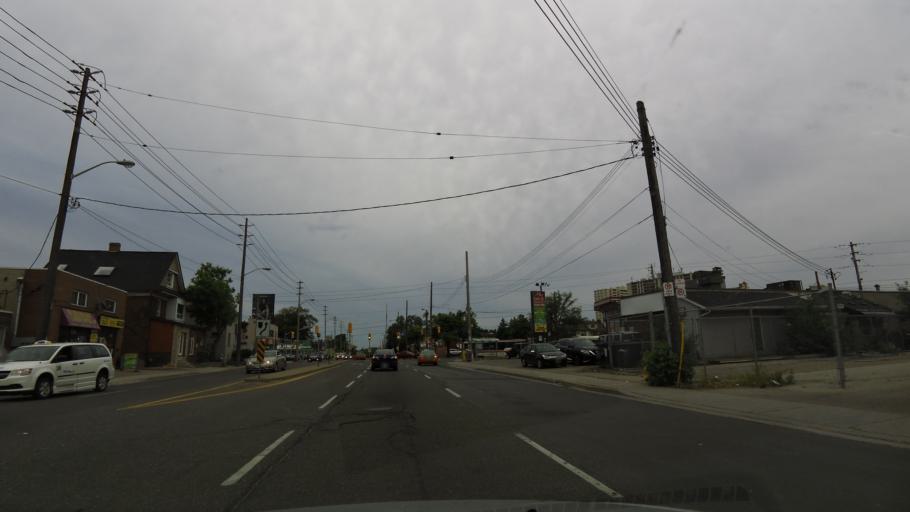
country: CA
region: Ontario
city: Etobicoke
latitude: 43.6922
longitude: -79.5011
